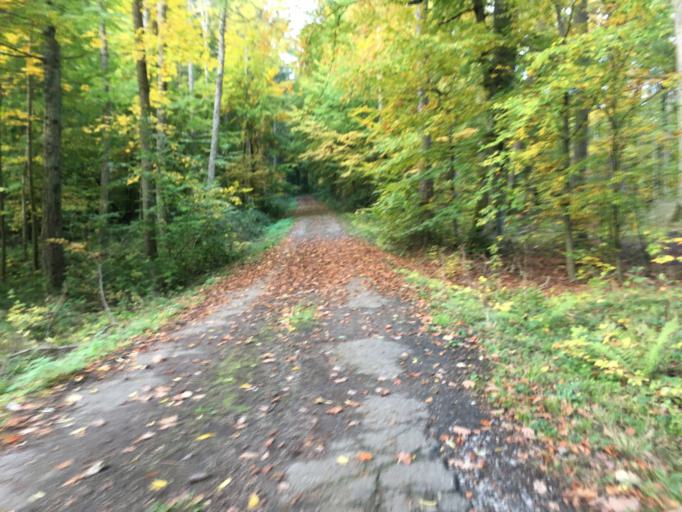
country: DE
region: Baden-Wuerttemberg
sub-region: Regierungsbezirk Stuttgart
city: Ittlingen
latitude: 49.2375
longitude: 8.9502
